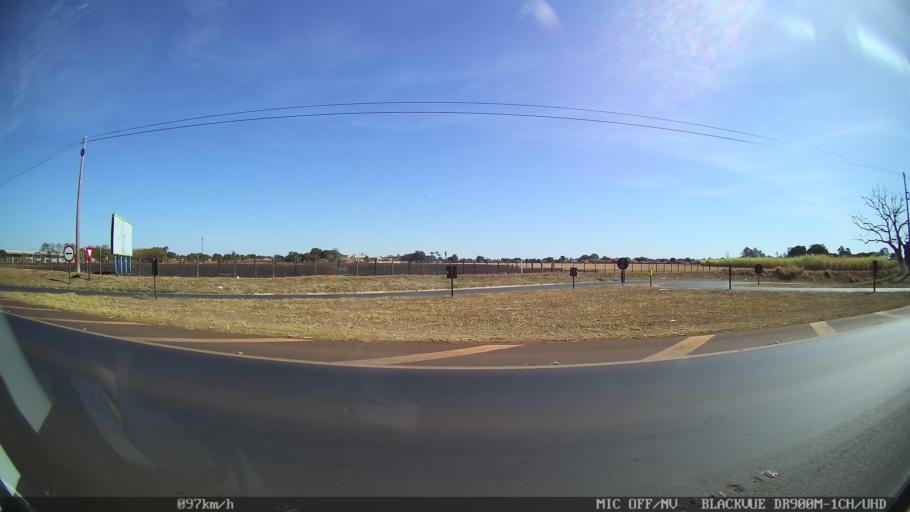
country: BR
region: Sao Paulo
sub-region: Barretos
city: Barretos
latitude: -20.5456
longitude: -48.5937
